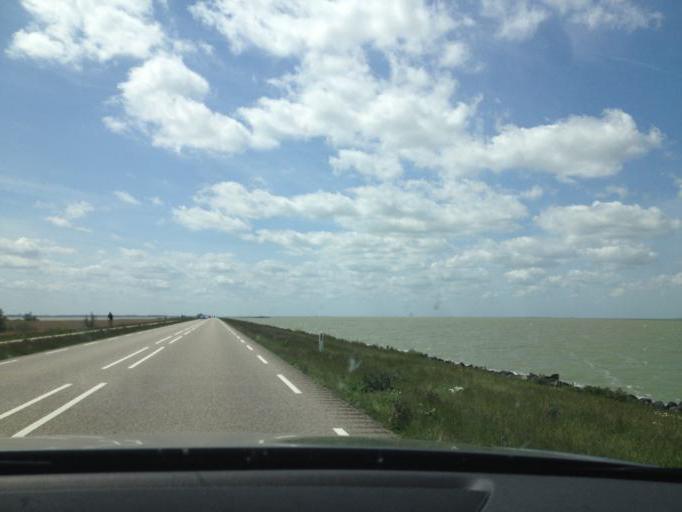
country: NL
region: Flevoland
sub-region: Gemeente Lelystad
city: Lelystad
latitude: 52.4796
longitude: 5.3616
